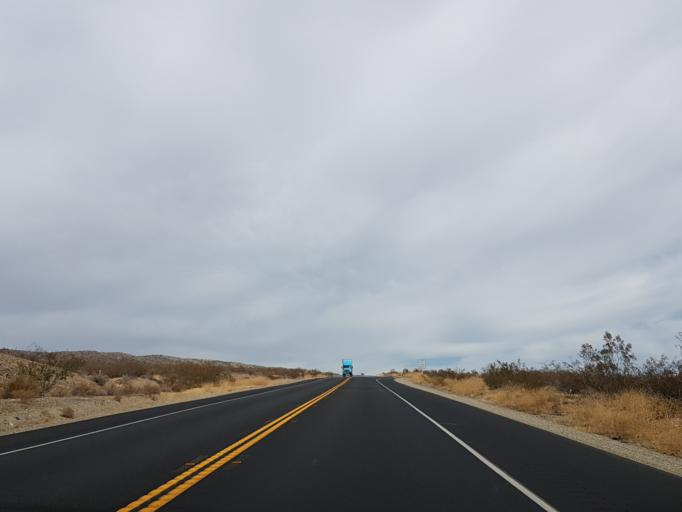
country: US
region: California
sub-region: Kern County
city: Ridgecrest
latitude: 35.4399
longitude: -117.6671
